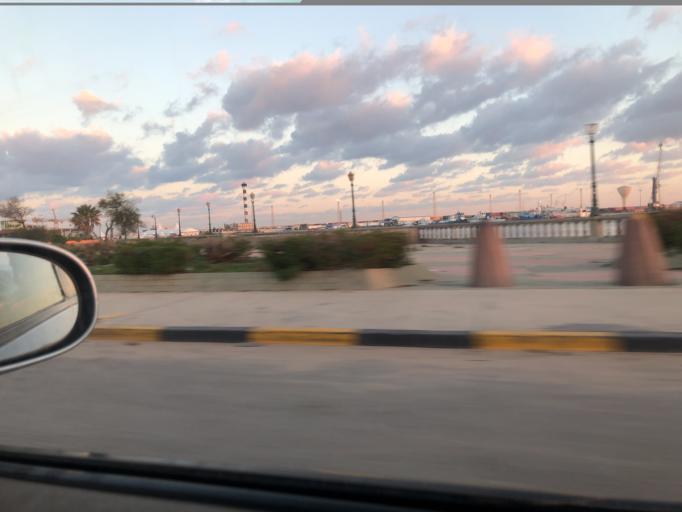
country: LY
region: Tripoli
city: Tripoli
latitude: 32.8985
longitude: 13.1795
